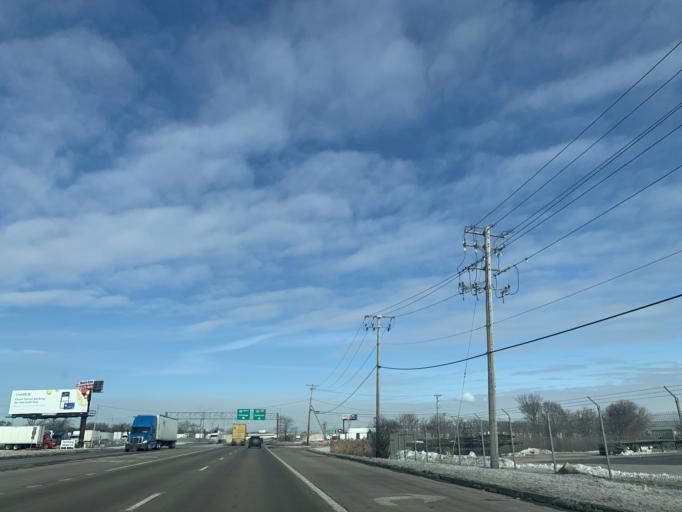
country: US
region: Illinois
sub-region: Will County
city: Bolingbrook
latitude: 41.6950
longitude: -88.0432
